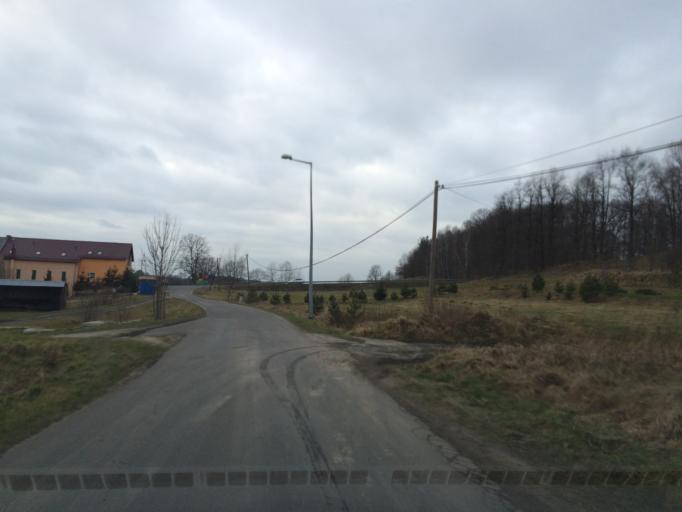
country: PL
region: Lower Silesian Voivodeship
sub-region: Powiat boleslawiecki
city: Boleslawiec
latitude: 51.1920
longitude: 15.5685
